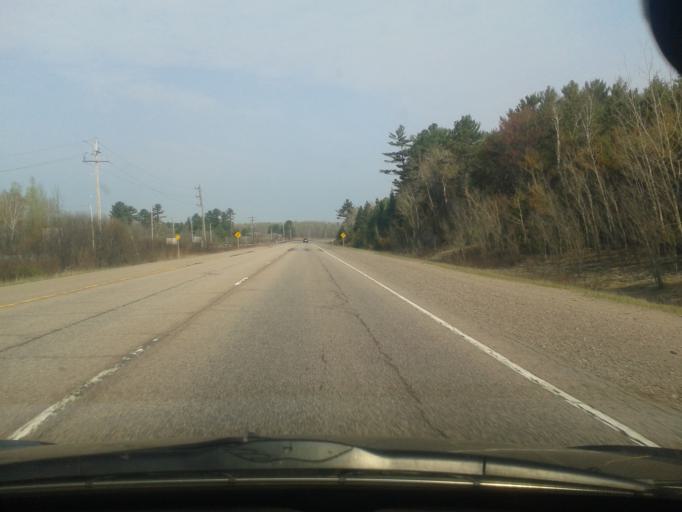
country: CA
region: Ontario
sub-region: Nipissing District
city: North Bay
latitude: 46.2863
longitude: -79.4132
